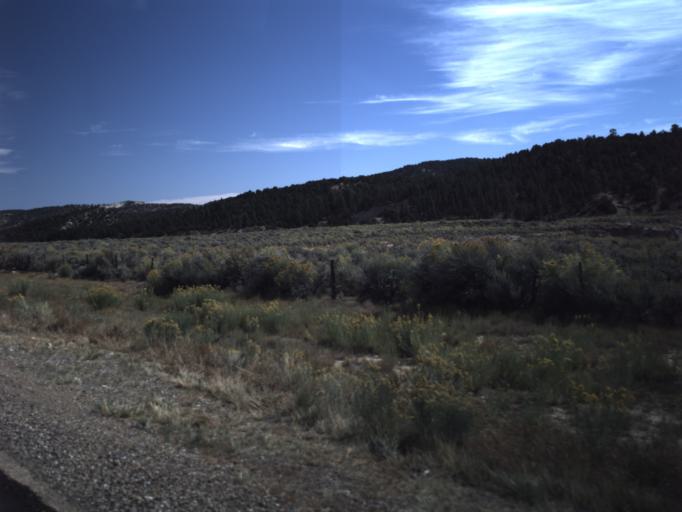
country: US
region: Utah
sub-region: Garfield County
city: Panguitch
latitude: 37.6741
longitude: -111.8270
